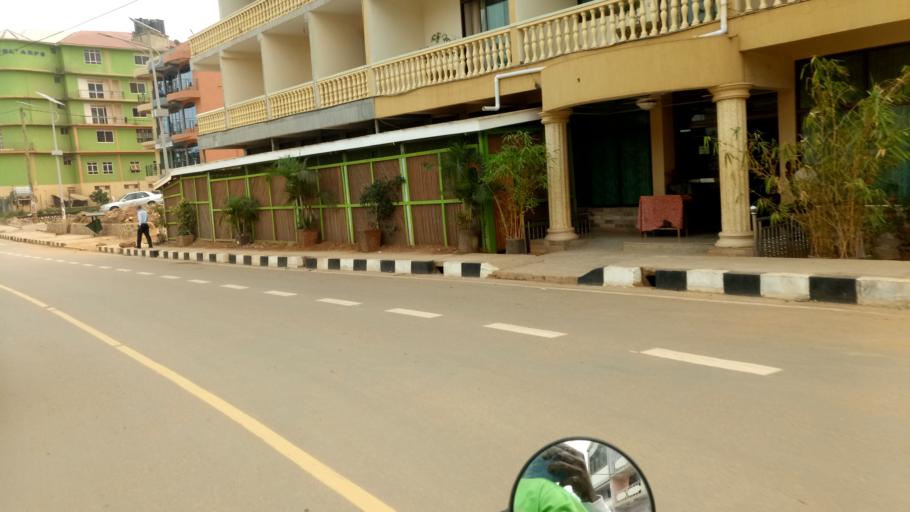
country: UG
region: Western Region
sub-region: Mbarara District
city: Mbarara
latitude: -0.6084
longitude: 30.6620
